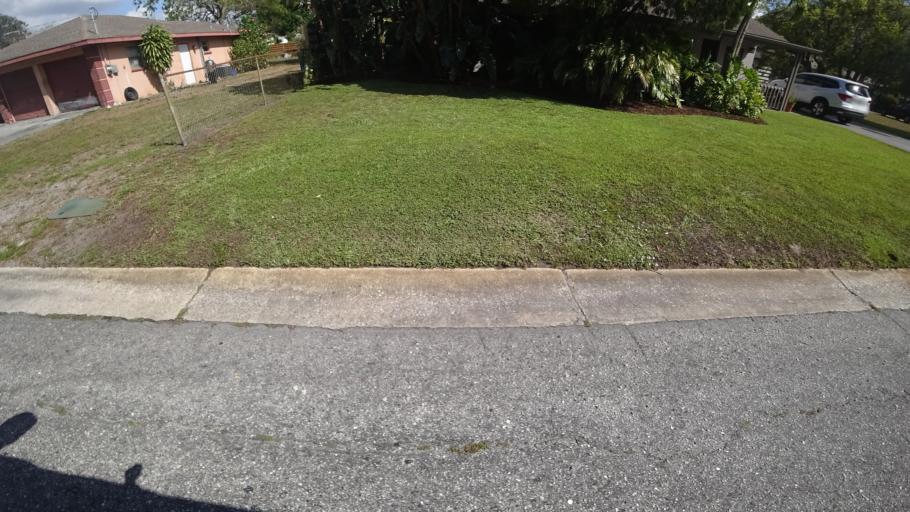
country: US
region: Florida
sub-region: Manatee County
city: Whitfield
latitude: 27.4225
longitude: -82.5730
